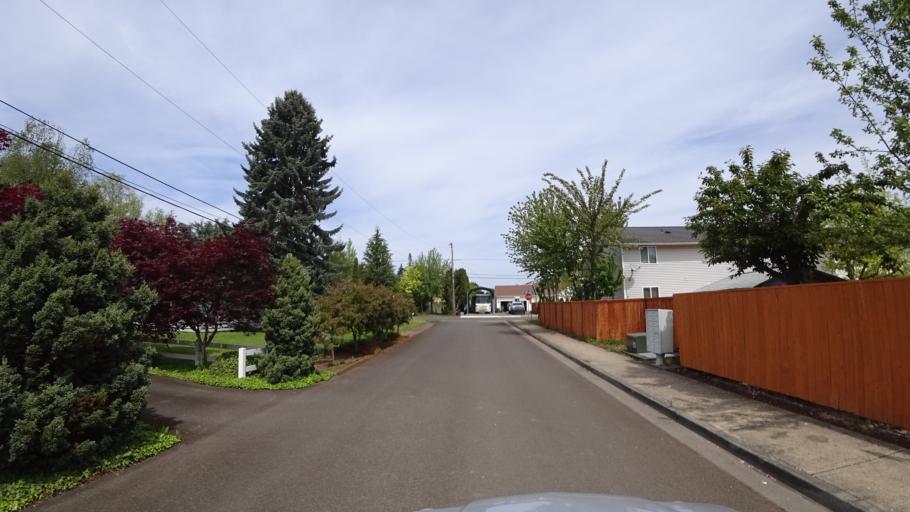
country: US
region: Oregon
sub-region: Washington County
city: Hillsboro
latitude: 45.5117
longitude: -122.9385
